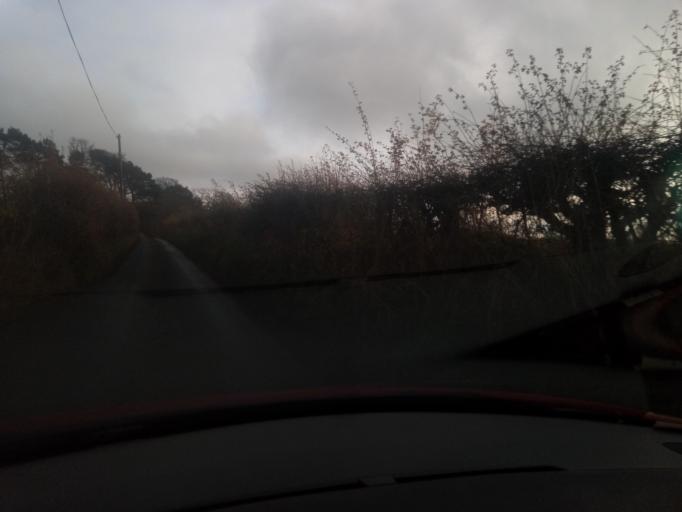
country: GB
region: Scotland
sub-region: The Scottish Borders
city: Jedburgh
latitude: 55.4855
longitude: -2.6100
